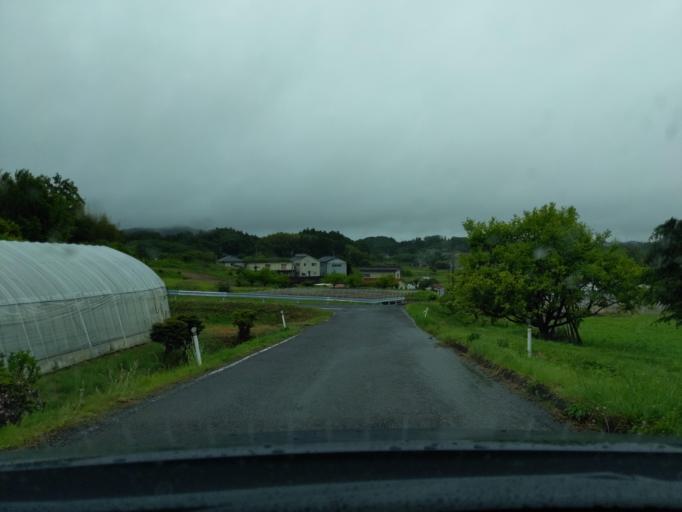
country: JP
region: Fukushima
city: Motomiya
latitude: 37.5010
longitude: 140.4536
